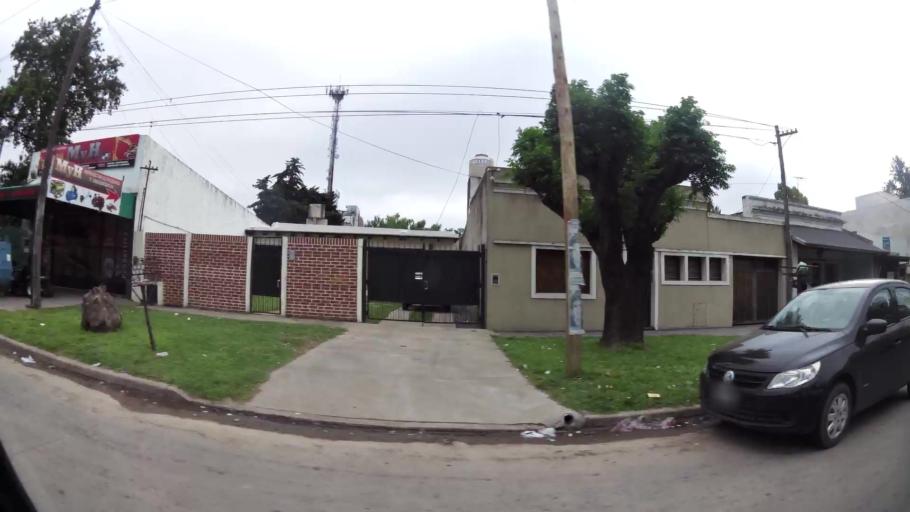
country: AR
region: Buenos Aires
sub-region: Partido de La Plata
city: La Plata
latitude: -34.9314
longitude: -57.9834
